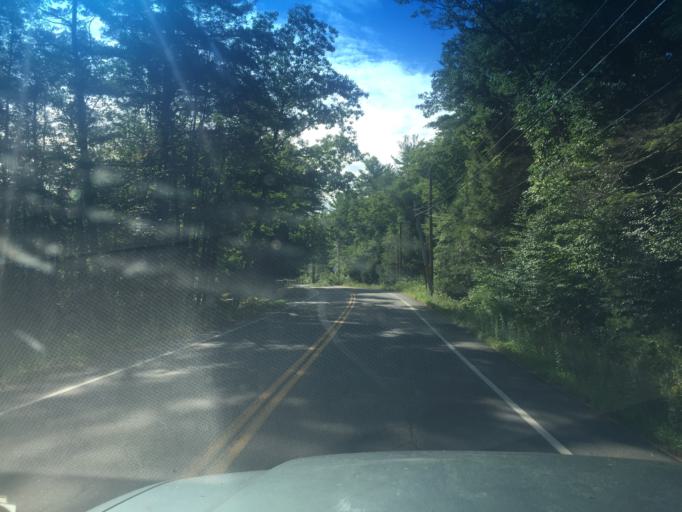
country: US
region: Maine
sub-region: York County
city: South Berwick
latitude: 43.2006
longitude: -70.7647
